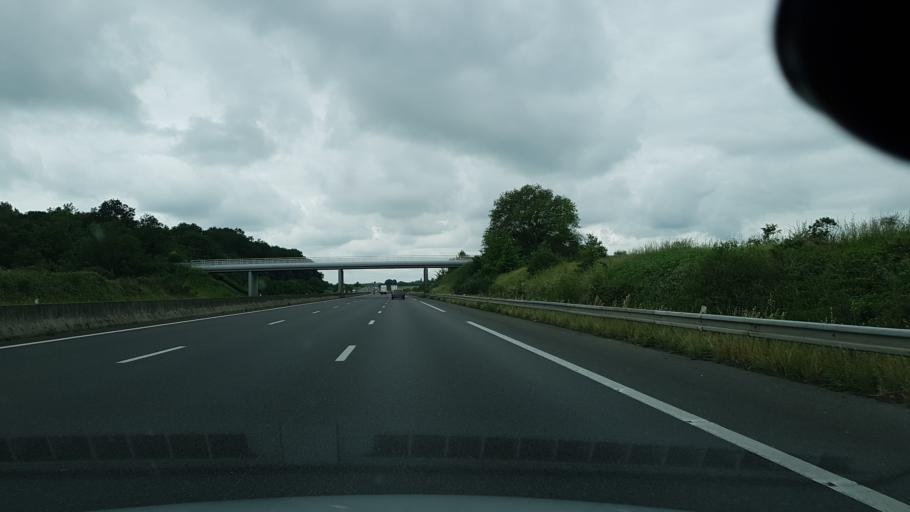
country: FR
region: Centre
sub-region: Departement du Loir-et-Cher
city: Herbault
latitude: 47.5971
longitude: 1.0997
